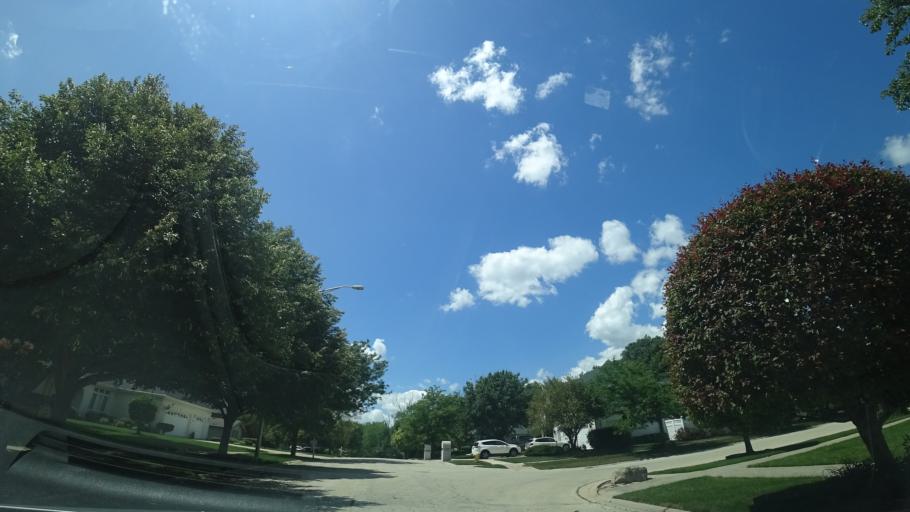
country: US
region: Illinois
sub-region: Cook County
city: Orland Hills
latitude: 41.5834
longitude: -87.8882
